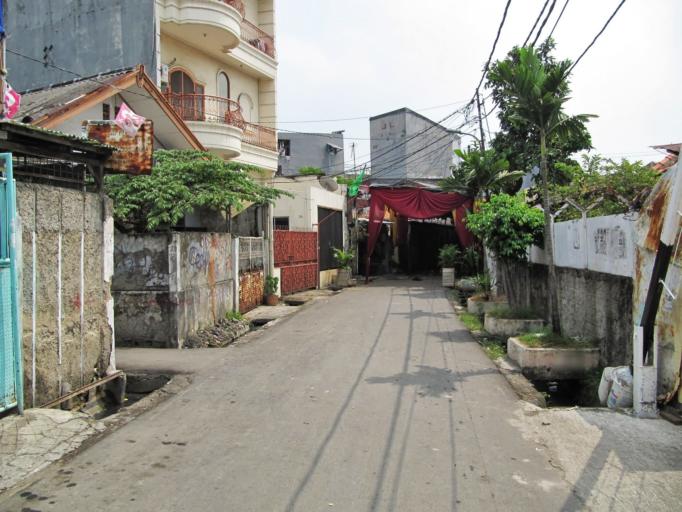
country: ID
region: Jakarta Raya
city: Jakarta
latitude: -6.1567
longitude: 106.8341
